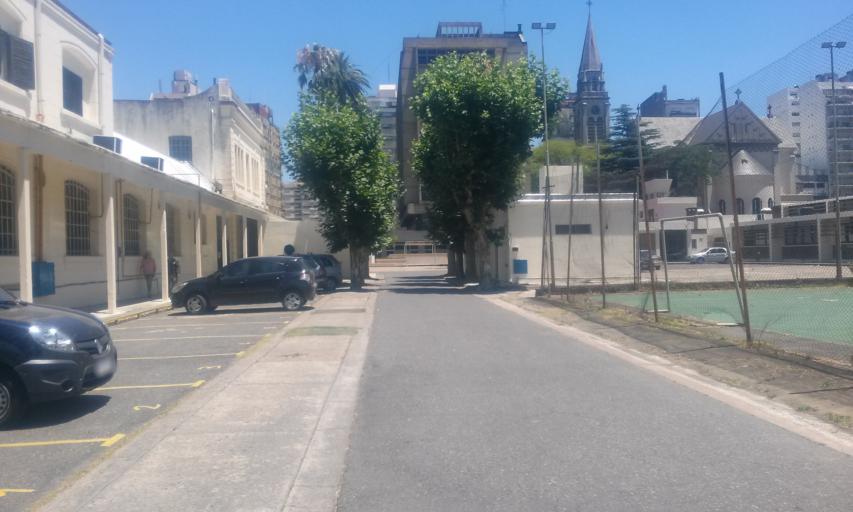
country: AR
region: Buenos Aires F.D.
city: Colegiales
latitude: -34.5712
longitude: -58.4396
